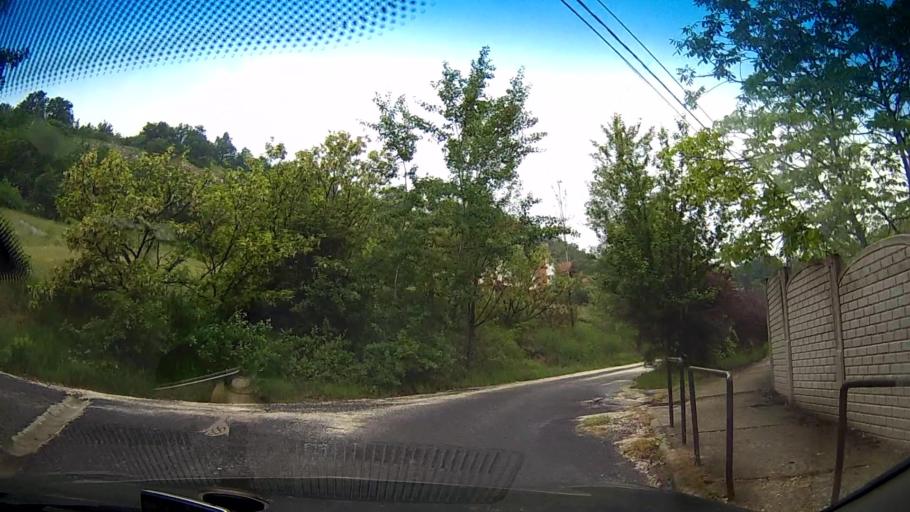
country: HU
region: Komarom-Esztergom
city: Piliscsev
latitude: 47.6592
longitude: 18.7920
